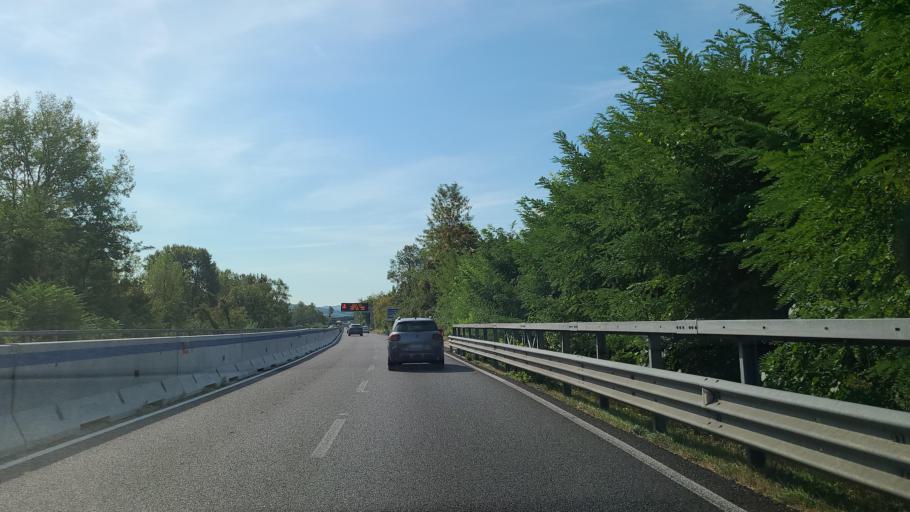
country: IT
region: Tuscany
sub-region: Province of Florence
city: Sambuca
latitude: 43.5975
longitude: 11.1947
